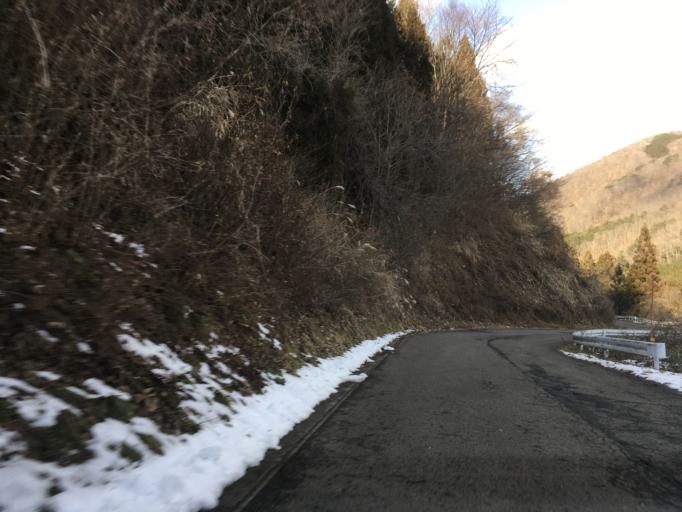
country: JP
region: Miyagi
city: Furukawa
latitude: 38.8122
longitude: 140.8322
